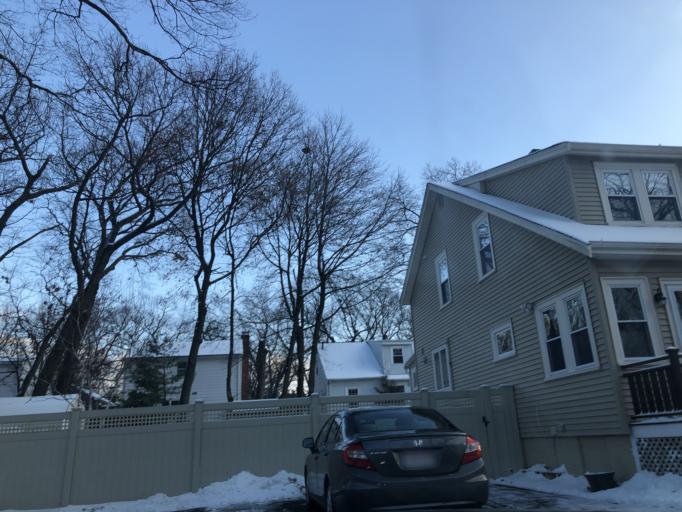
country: US
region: Massachusetts
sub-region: Middlesex County
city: Arlington
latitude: 42.4281
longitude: -71.1685
